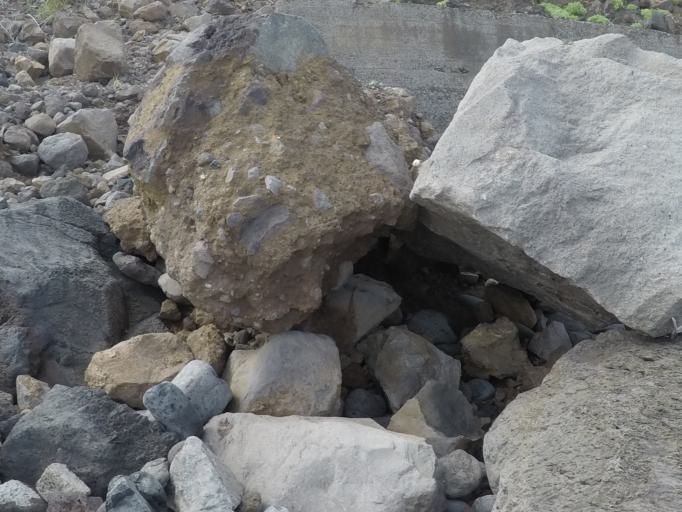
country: PT
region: Madeira
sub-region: Sao Vicente
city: Sao Vicente
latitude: 32.8221
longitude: -17.0039
